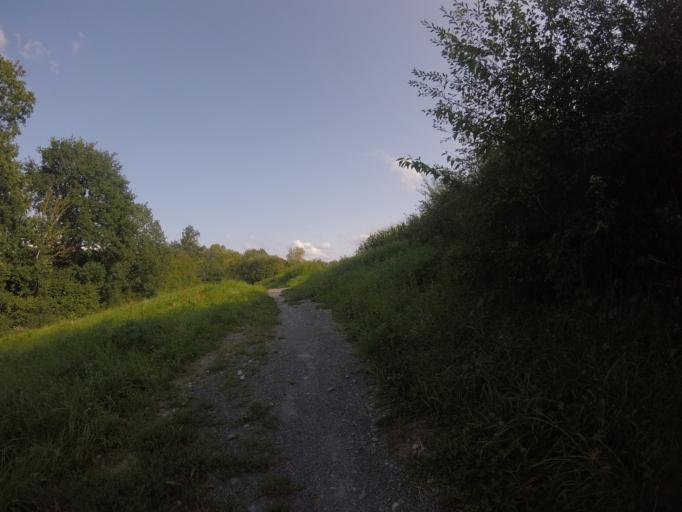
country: DE
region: Baden-Wuerttemberg
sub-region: Regierungsbezirk Stuttgart
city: Mittelschontal
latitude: 48.9547
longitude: 9.3943
